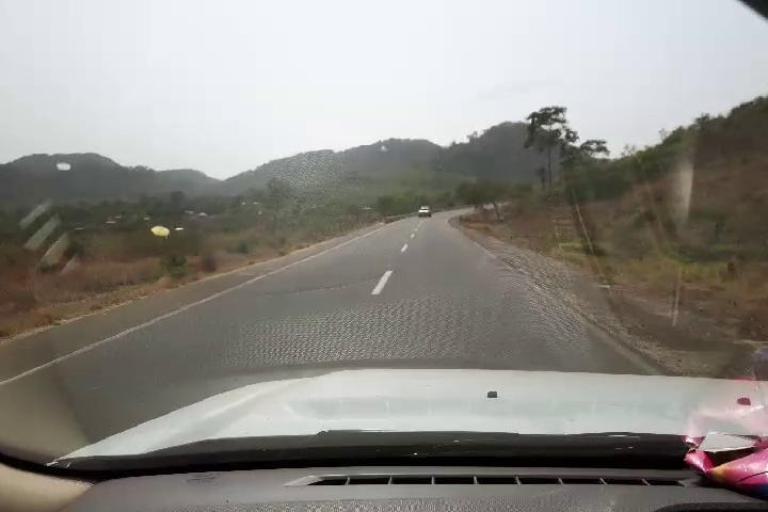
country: SL
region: Western Area
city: Waterloo
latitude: 8.2059
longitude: -13.1304
